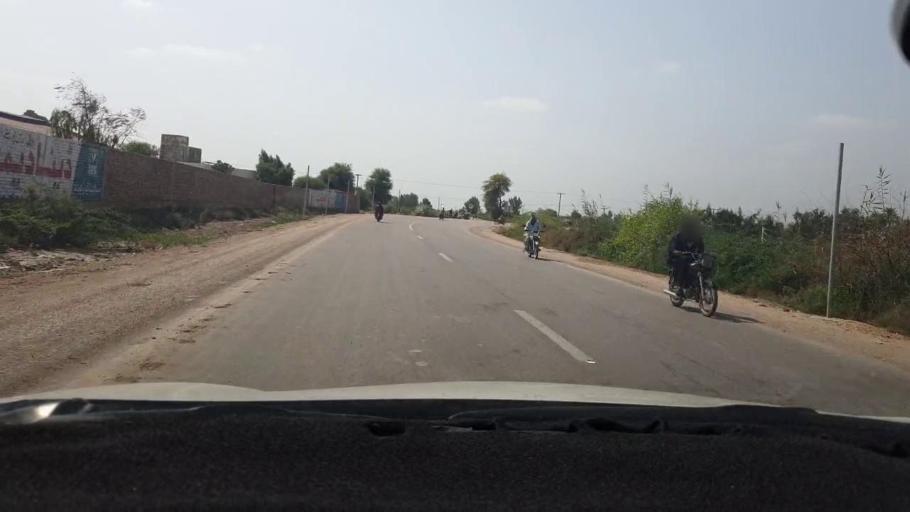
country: PK
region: Sindh
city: Mirpur Khas
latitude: 25.5719
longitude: 69.0694
